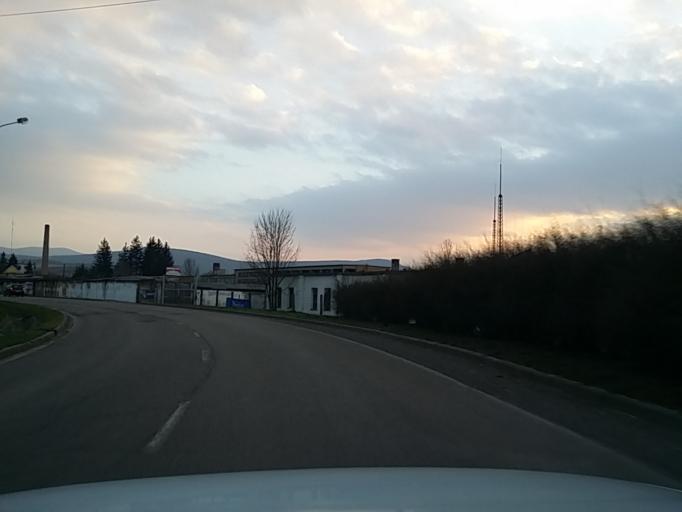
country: HU
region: Nograd
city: Batonyterenye
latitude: 47.9840
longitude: 19.8239
